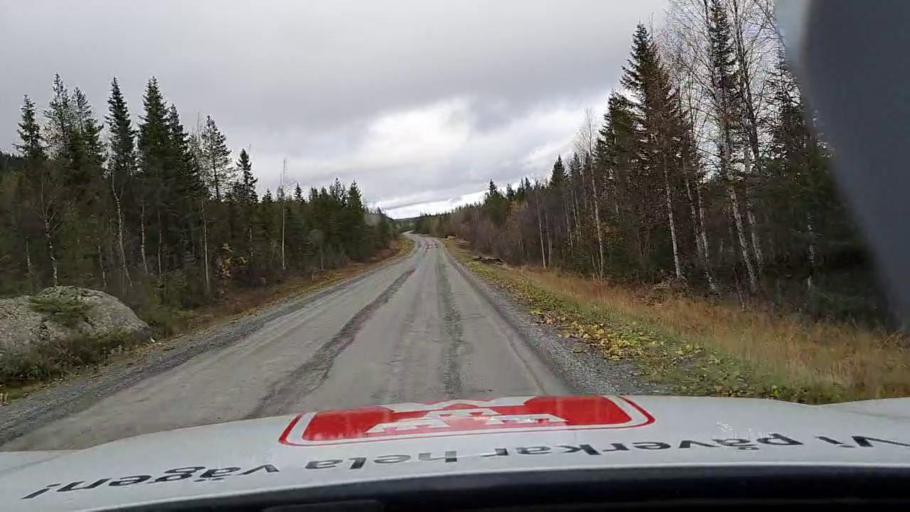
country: SE
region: Jaemtland
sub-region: Krokoms Kommun
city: Valla
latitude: 63.0581
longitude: 13.9627
